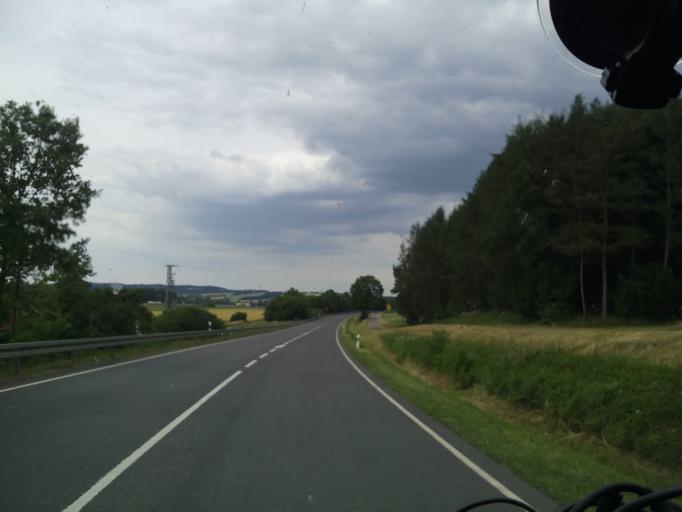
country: DE
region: Bavaria
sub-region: Regierungsbezirk Unterfranken
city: Untermerzbach
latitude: 50.1143
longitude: 10.8689
